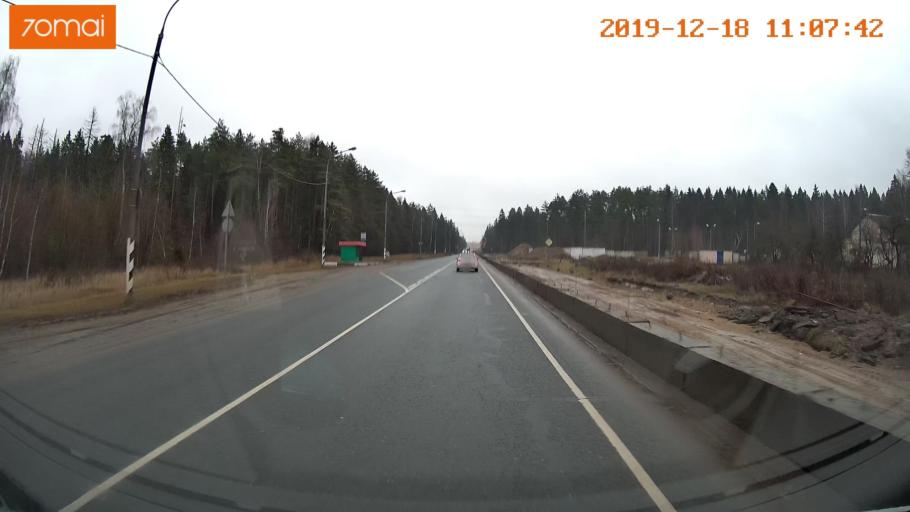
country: RU
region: Moskovskaya
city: Golitsyno
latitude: 55.6164
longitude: 37.0111
